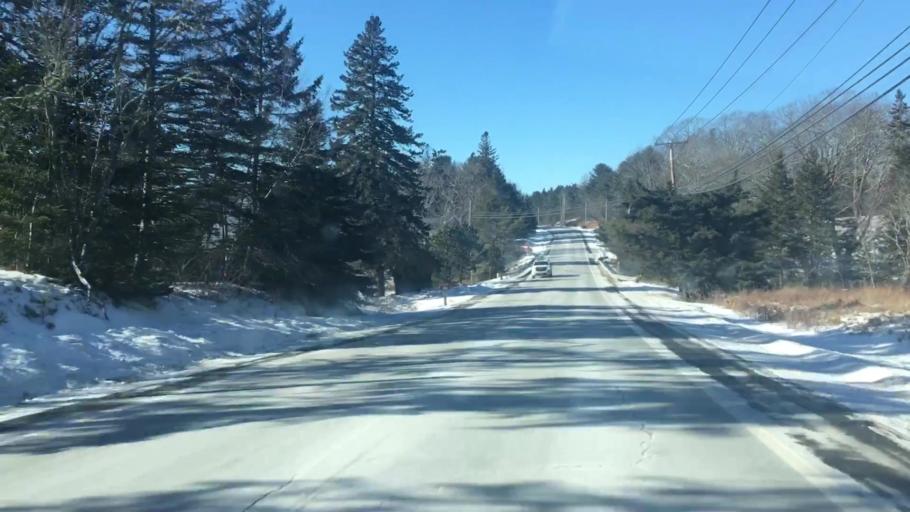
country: US
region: Maine
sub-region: Hancock County
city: Surry
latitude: 44.4938
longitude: -68.4656
